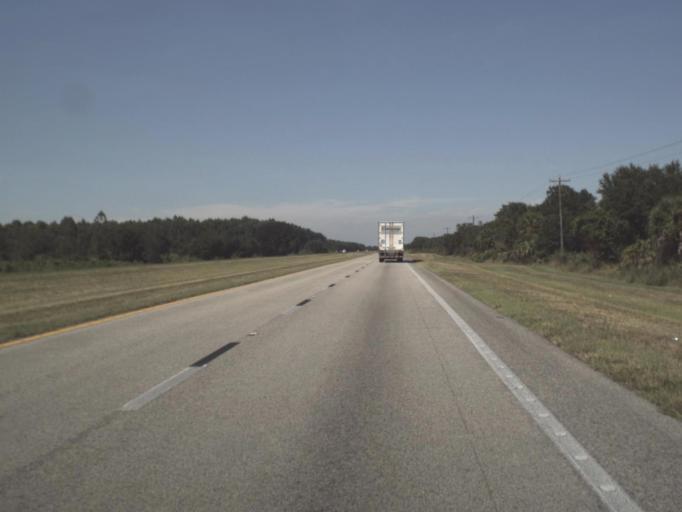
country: US
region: Florida
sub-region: Hendry County
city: Port LaBelle
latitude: 26.9895
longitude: -81.3248
